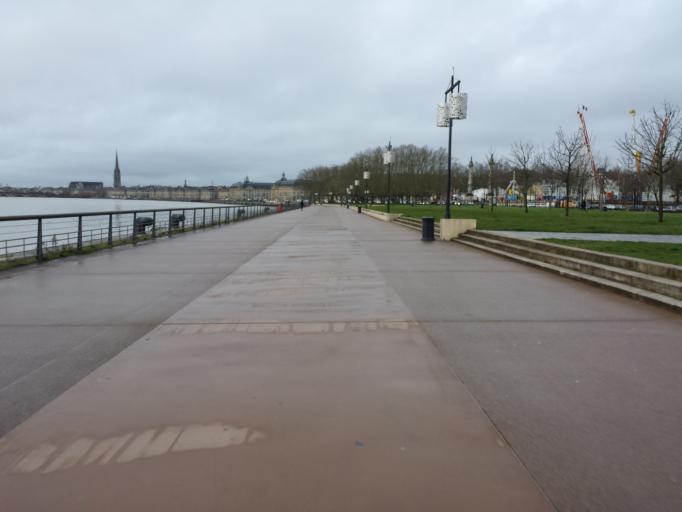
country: FR
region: Aquitaine
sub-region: Departement de la Gironde
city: Bordeaux
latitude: 44.8484
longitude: -0.5699
